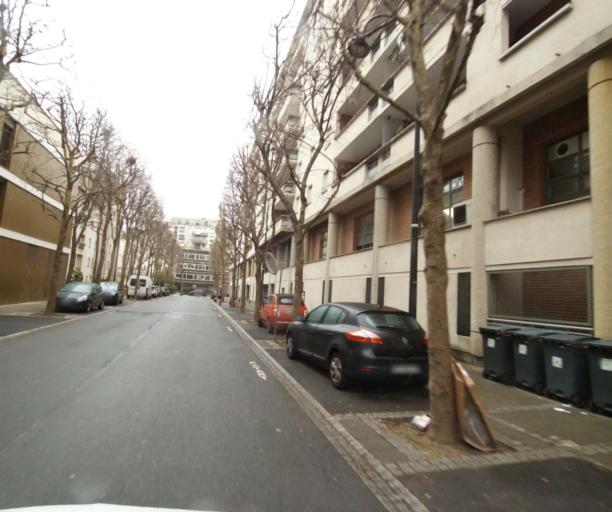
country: FR
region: Ile-de-France
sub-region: Departement des Yvelines
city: Chatou
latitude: 48.8891
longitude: 2.1702
